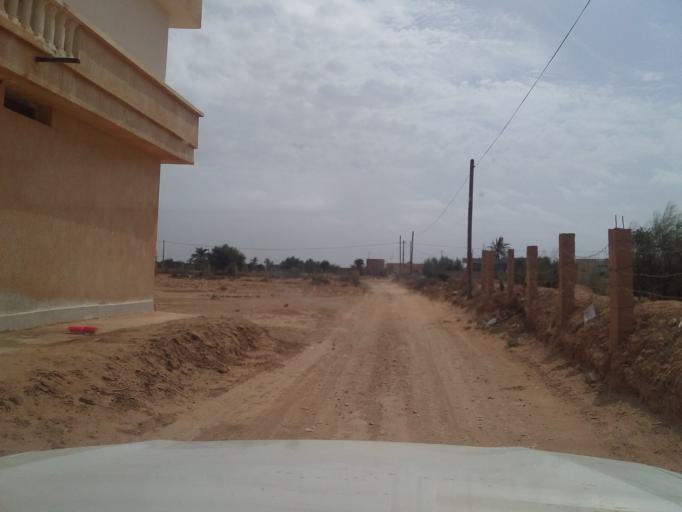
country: TN
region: Qabis
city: Matmata
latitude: 33.6185
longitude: 10.2629
